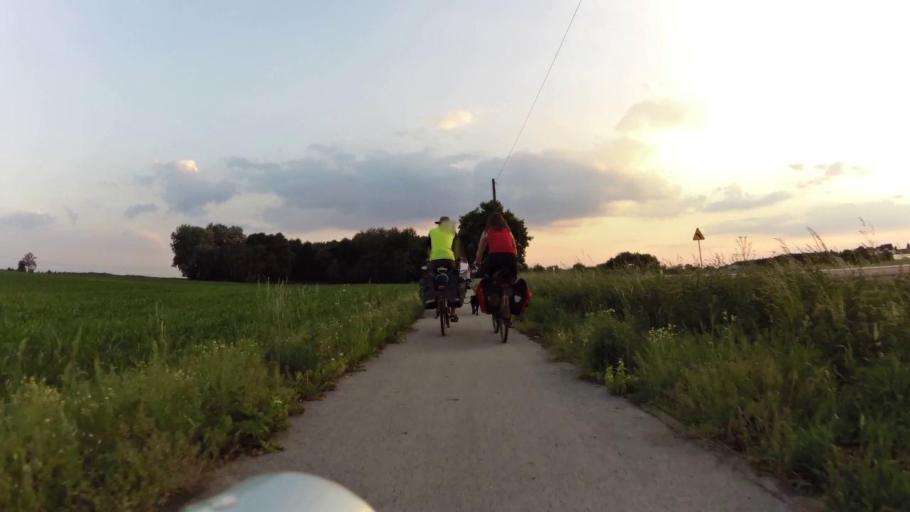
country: PL
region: Kujawsko-Pomorskie
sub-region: Powiat bydgoski
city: Dabrowa Chelminska
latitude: 53.1621
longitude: 18.2455
